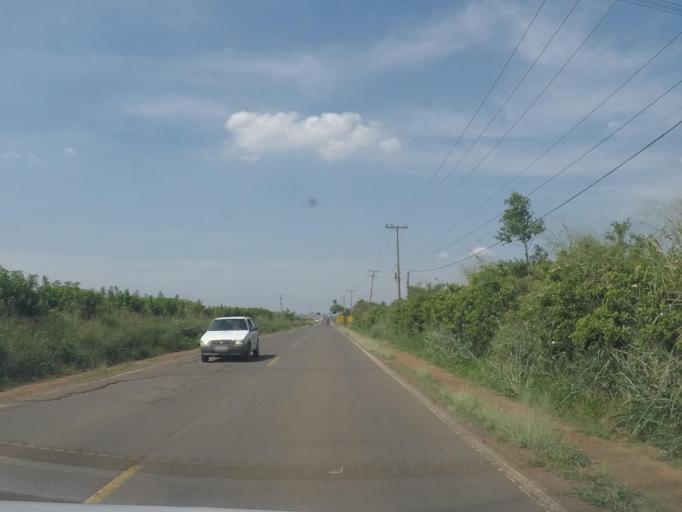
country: BR
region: Sao Paulo
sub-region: Sumare
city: Sumare
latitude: -22.8644
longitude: -47.2947
